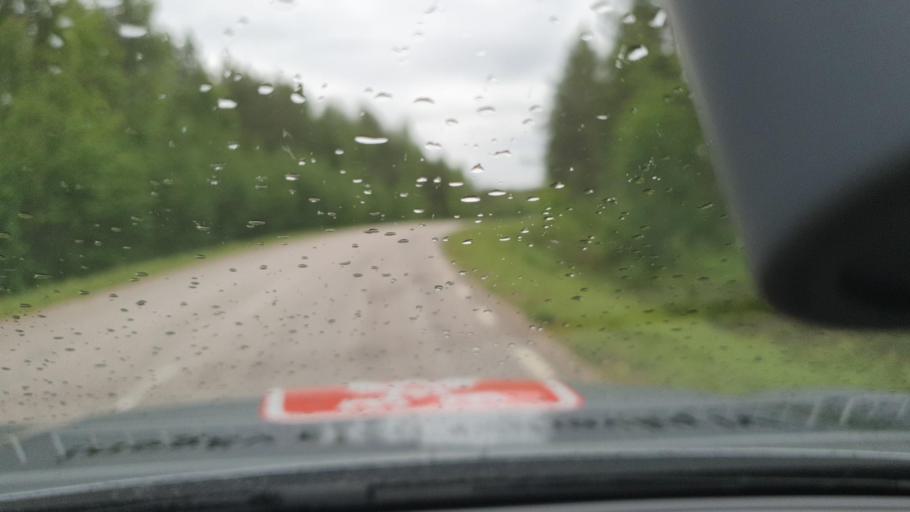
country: SE
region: Norrbotten
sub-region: Overkalix Kommun
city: OEverkalix
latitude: 66.3589
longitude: 22.8017
